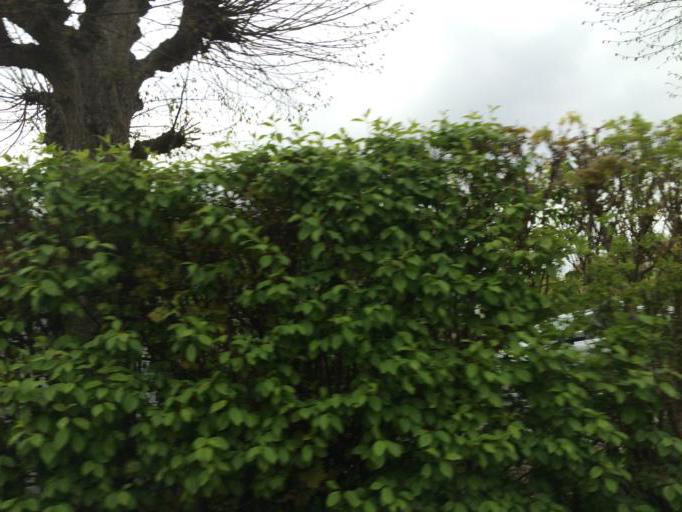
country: SE
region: Soedermanland
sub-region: Eskilstuna Kommun
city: Kvicksund
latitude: 59.4512
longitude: 16.3278
